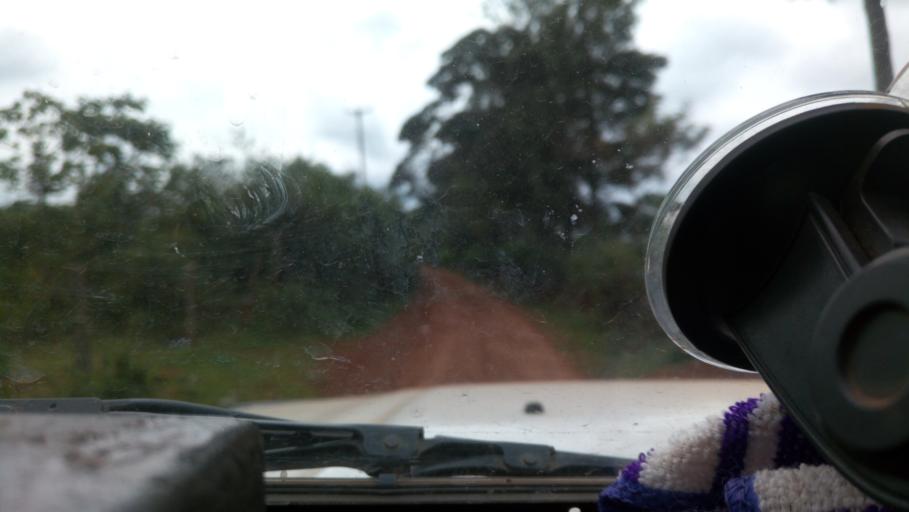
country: KE
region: Kericho
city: Litein
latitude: -0.5378
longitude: 35.1298
